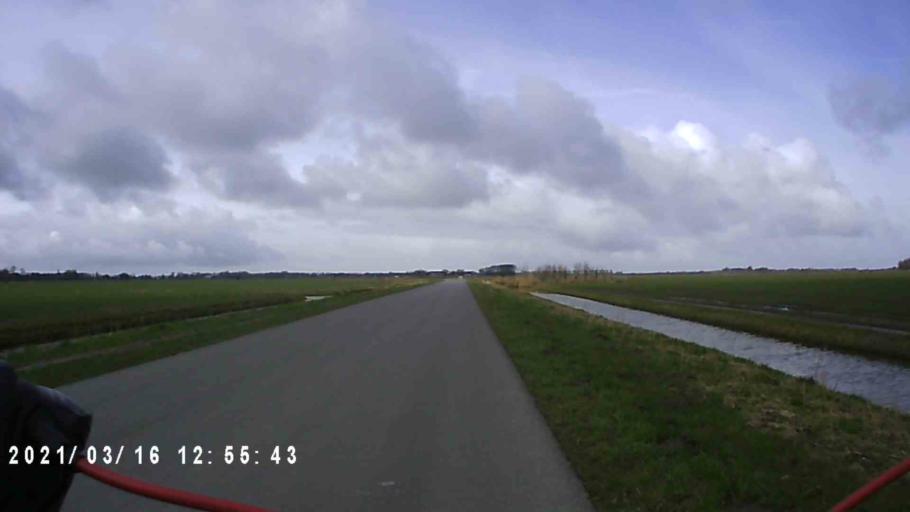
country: NL
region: Friesland
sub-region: Menameradiel
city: Berltsum
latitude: 53.2544
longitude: 5.6651
